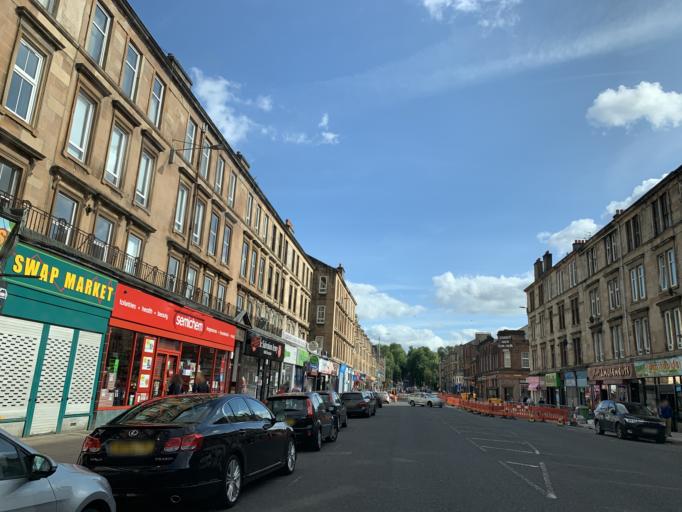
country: GB
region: Scotland
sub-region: Glasgow City
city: Glasgow
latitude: 55.8362
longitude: -4.2648
